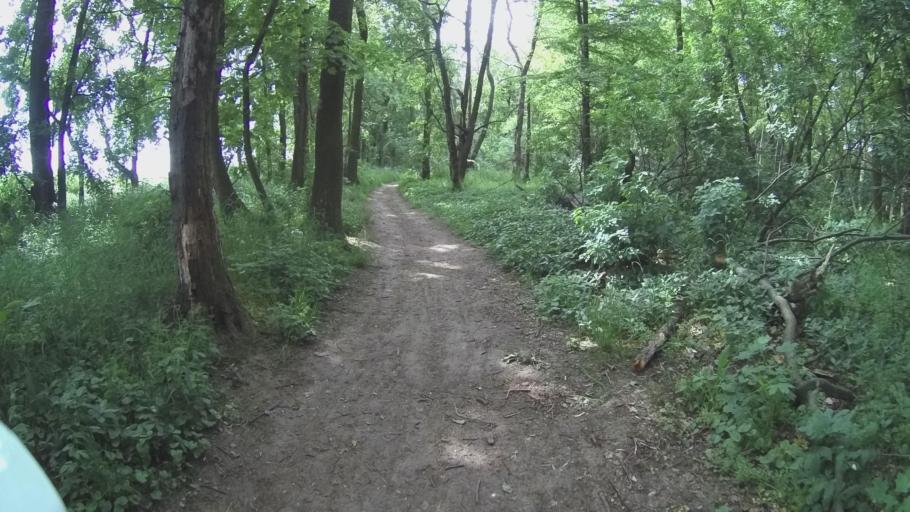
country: CZ
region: Central Bohemia
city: Zdiby
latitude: 50.1742
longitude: 14.4719
